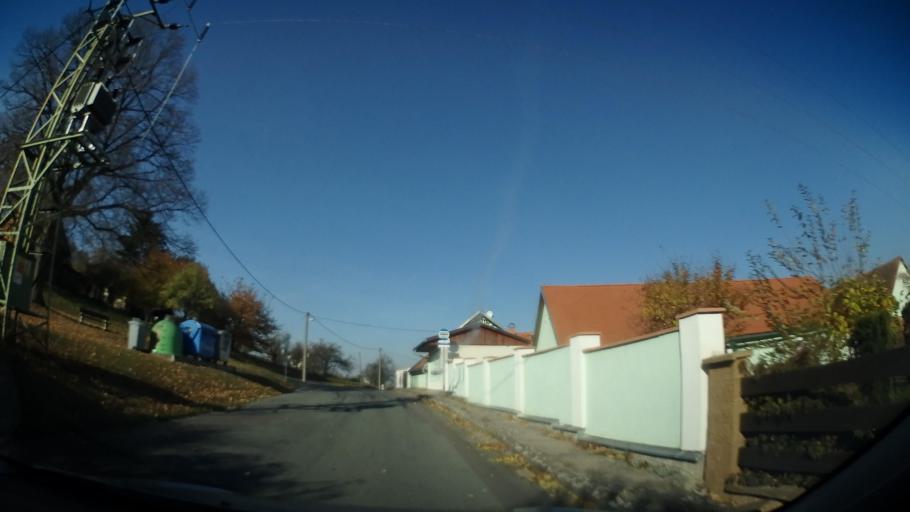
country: CZ
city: Ceske Mezirici
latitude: 50.2413
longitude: 16.0238
